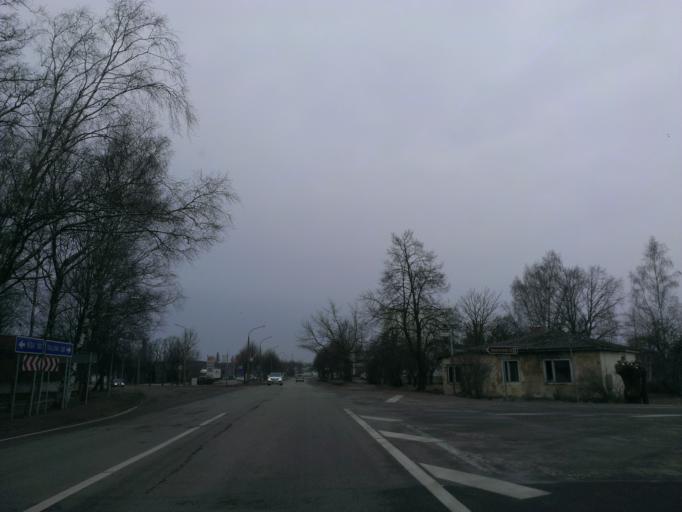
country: LV
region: Salacgrivas
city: Salacgriva
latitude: 57.7493
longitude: 24.3585
